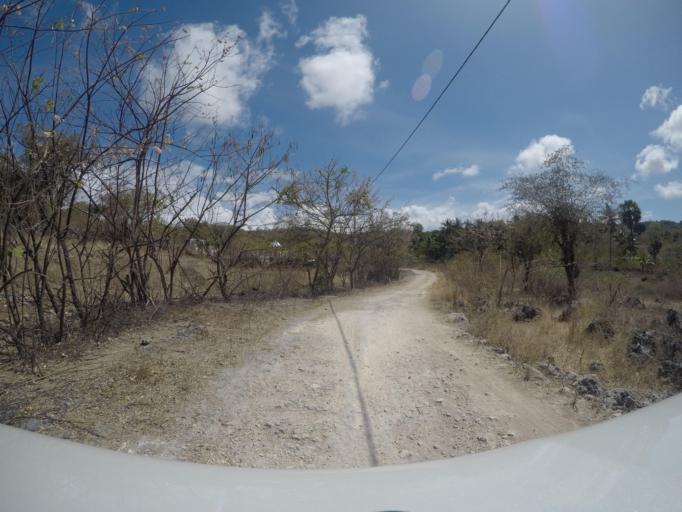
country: TL
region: Baucau
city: Baucau
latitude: -8.4448
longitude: 126.4381
